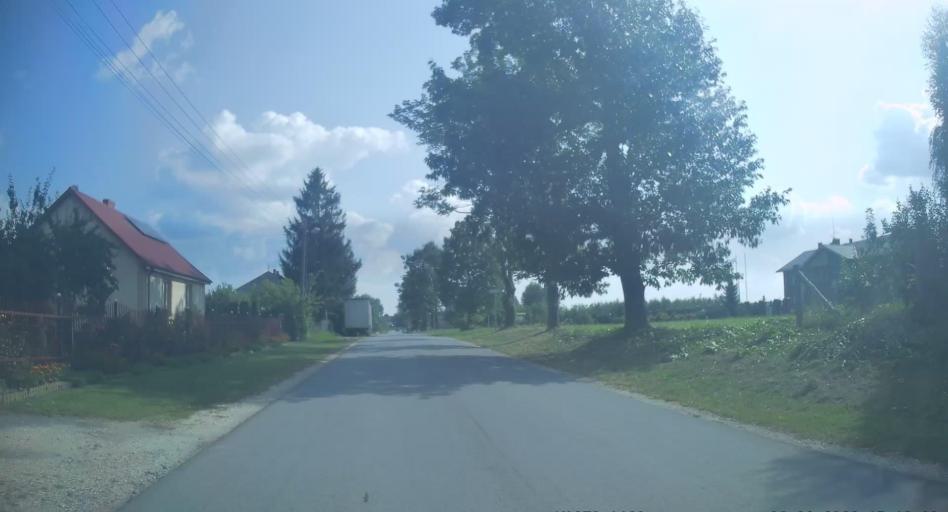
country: PL
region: Swietokrzyskie
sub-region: Powiat konecki
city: Radoszyce
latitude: 51.0836
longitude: 20.2581
